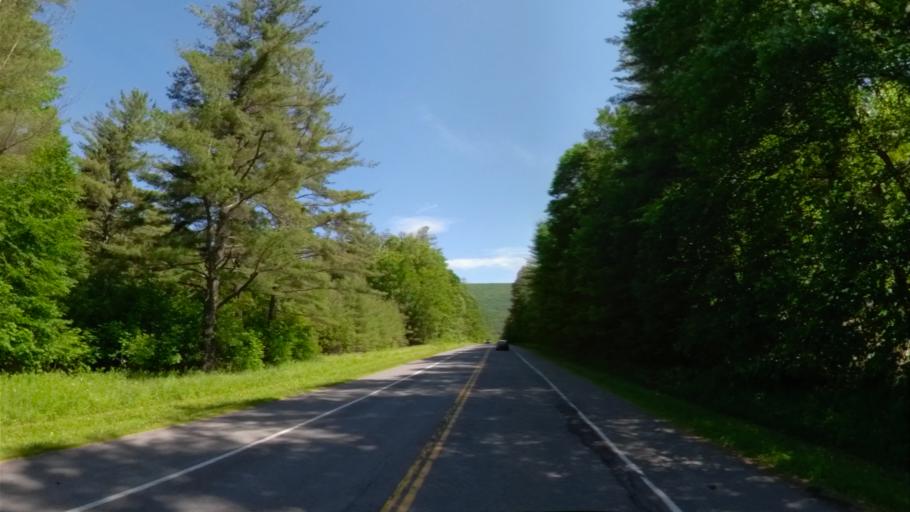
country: US
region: New York
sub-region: Ulster County
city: Shokan
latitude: 42.1055
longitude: -74.4328
